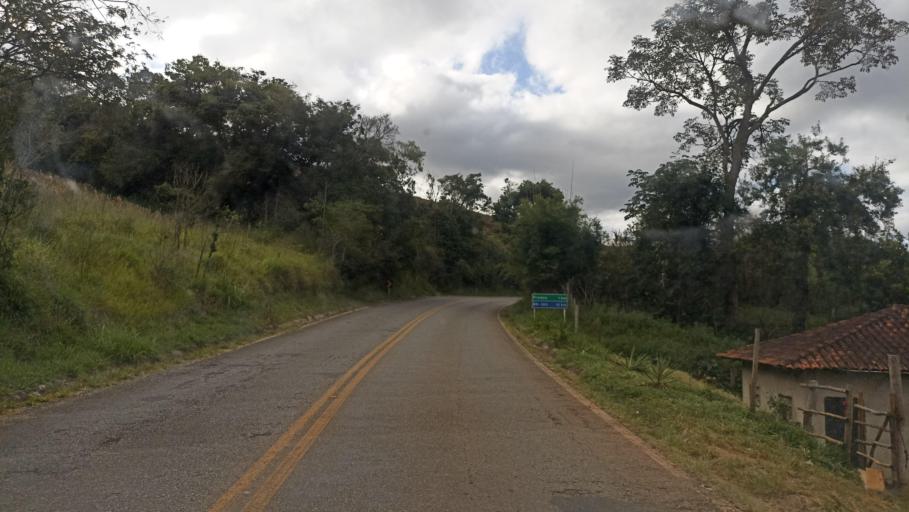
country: BR
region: Minas Gerais
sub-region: Tiradentes
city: Tiradentes
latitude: -21.0806
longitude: -44.0748
